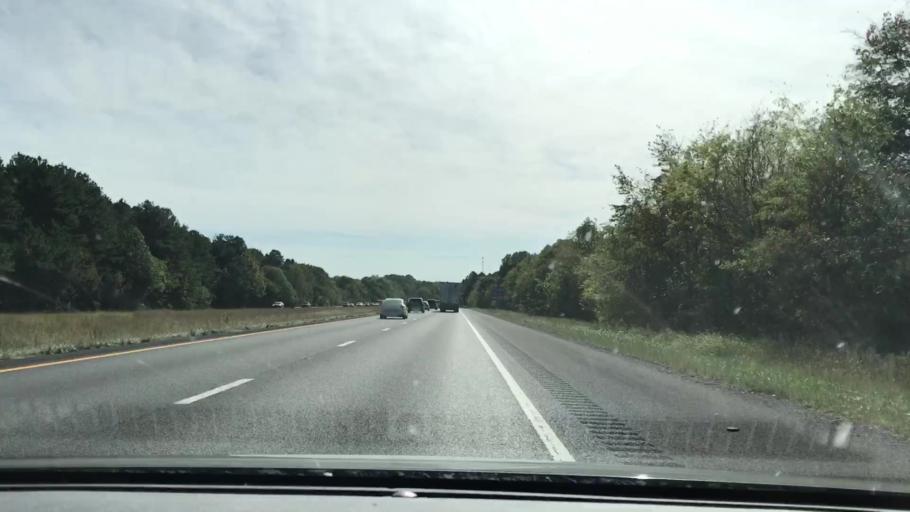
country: US
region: Tennessee
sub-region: Sumner County
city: White House
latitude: 36.4933
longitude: -86.6714
